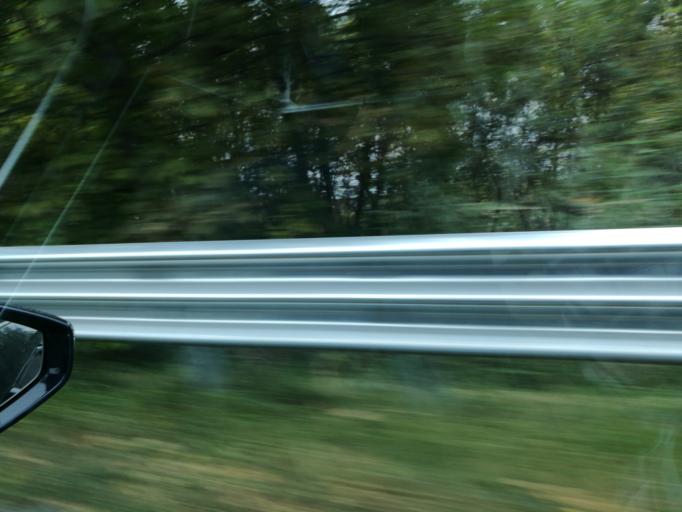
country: RO
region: Tulcea
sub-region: Oras Macin
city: Macin
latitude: 45.2591
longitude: 28.0814
